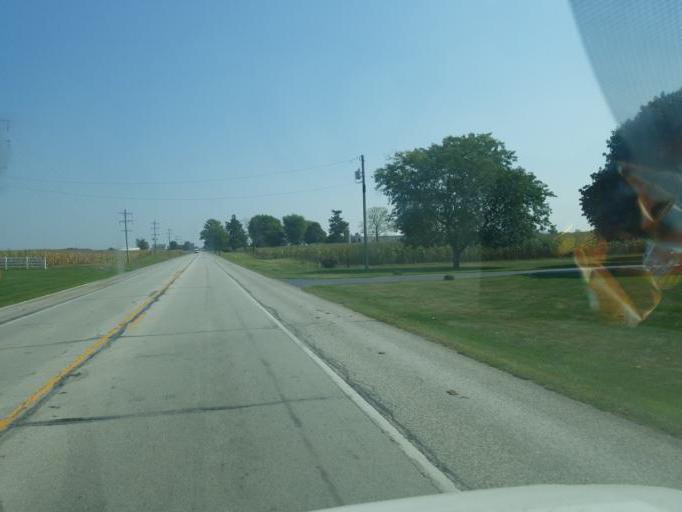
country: US
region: Indiana
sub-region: LaGrange County
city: Topeka
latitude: 41.6405
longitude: -85.5289
